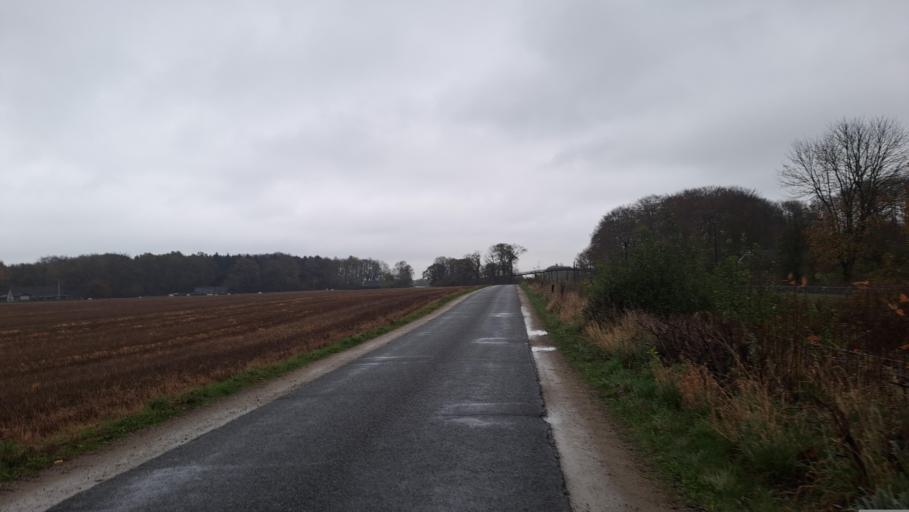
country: DK
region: Central Jutland
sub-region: Hedensted Kommune
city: Hedensted
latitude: 55.8198
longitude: 9.7182
